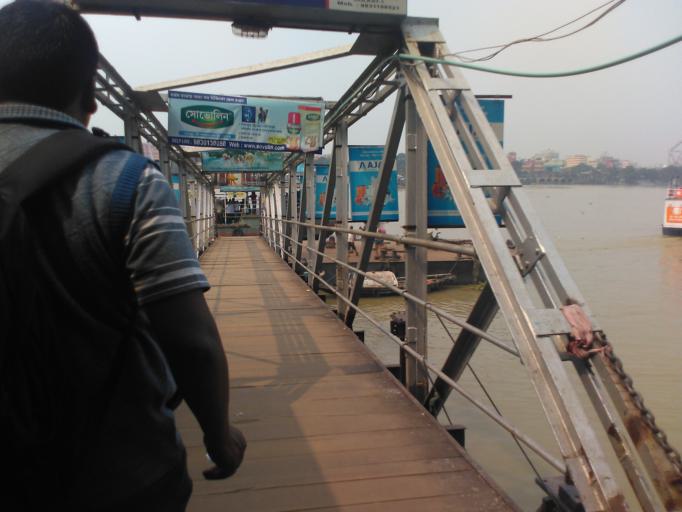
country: IN
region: West Bengal
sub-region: Kolkata
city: Bara Bazar
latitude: 22.5804
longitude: 88.3474
